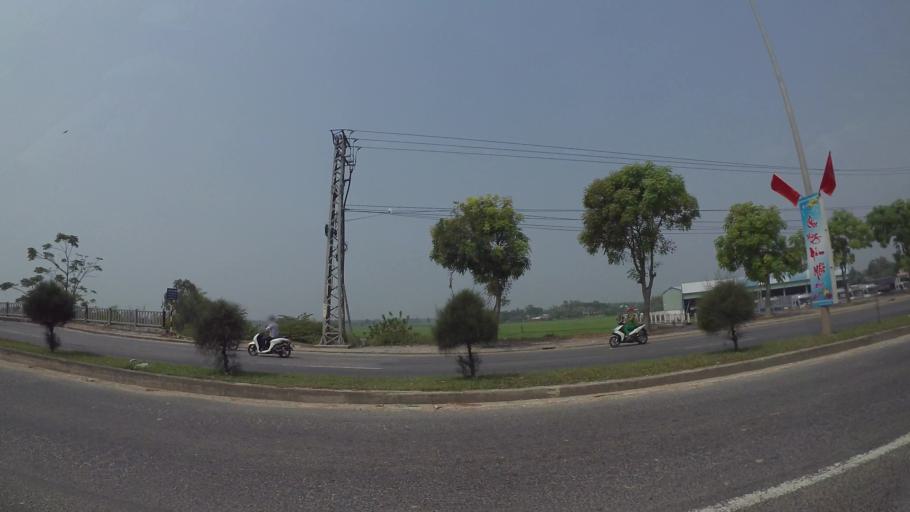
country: VN
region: Da Nang
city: Cam Le
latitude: 15.9732
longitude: 108.2087
